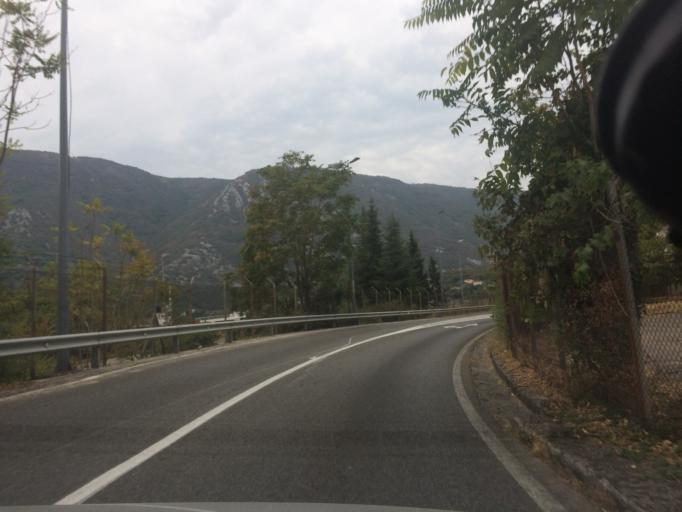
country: ME
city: Lipci
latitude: 42.4972
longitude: 18.6582
